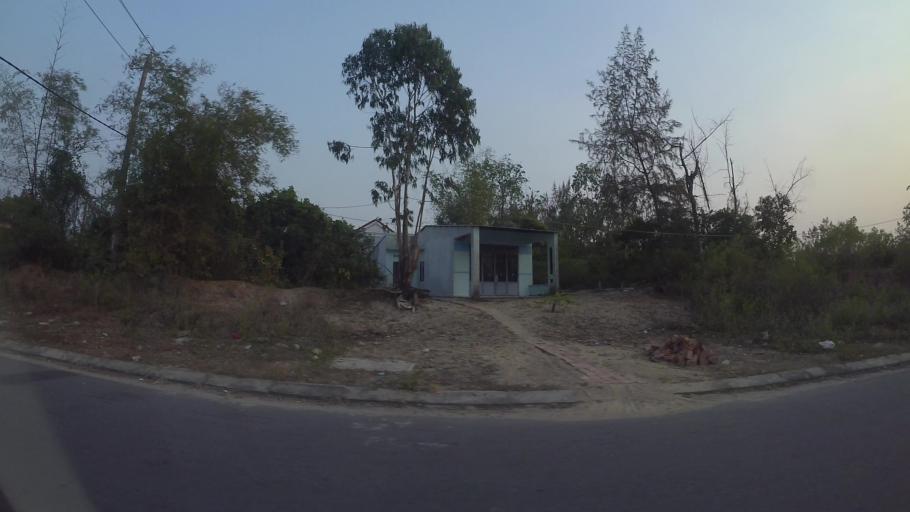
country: VN
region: Da Nang
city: Ngu Hanh Son
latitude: 15.9777
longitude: 108.2386
